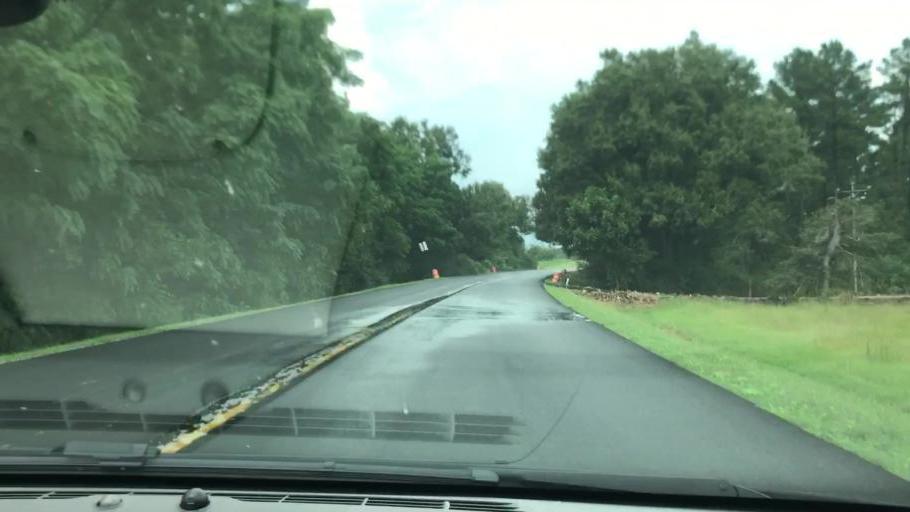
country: US
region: Georgia
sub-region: Early County
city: Blakely
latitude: 31.4064
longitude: -84.9612
